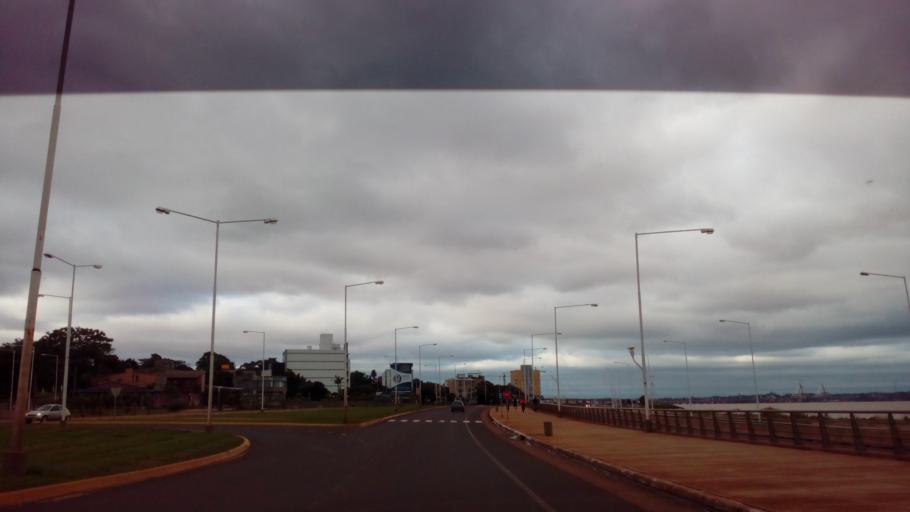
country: AR
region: Misiones
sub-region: Departamento de Capital
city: Posadas
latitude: -27.3924
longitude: -55.8921
